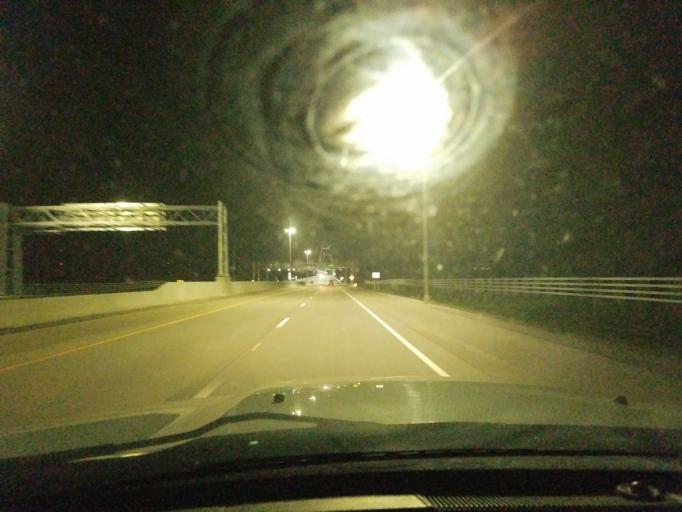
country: US
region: Kentucky
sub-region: Jefferson County
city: Prospect
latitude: 38.3342
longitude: -85.6332
